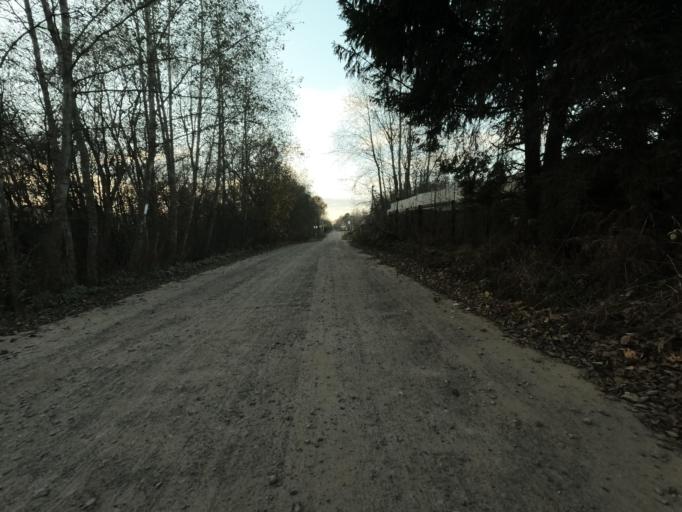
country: RU
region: Leningrad
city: Mga
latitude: 59.7641
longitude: 31.2497
